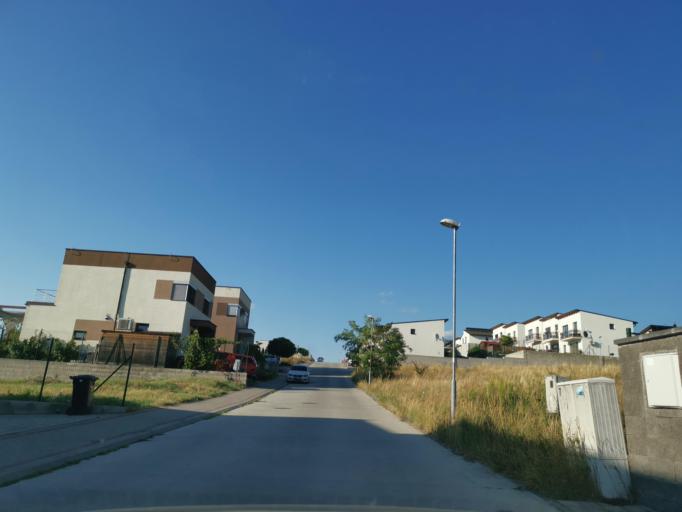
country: SK
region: Bratislavsky
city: Stupava
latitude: 48.2821
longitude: 17.0441
